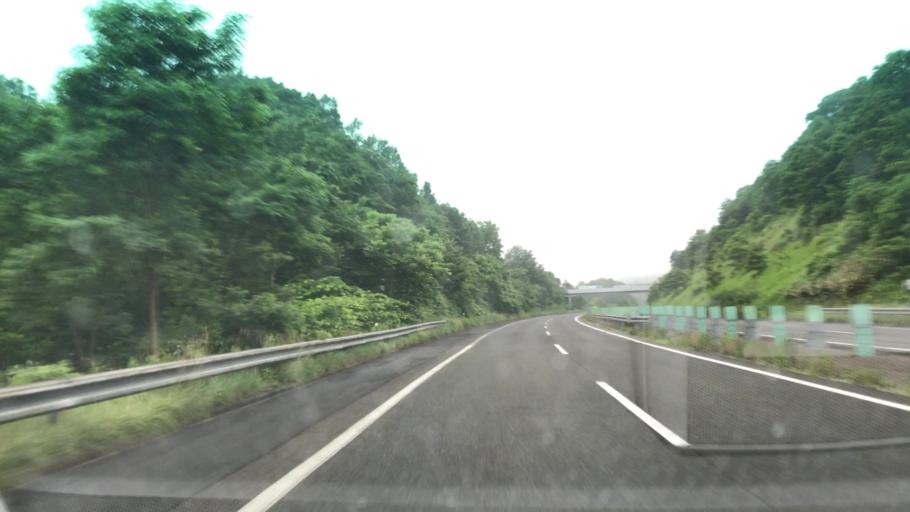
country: JP
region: Hokkaido
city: Shiraoi
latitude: 42.4882
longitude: 141.2344
